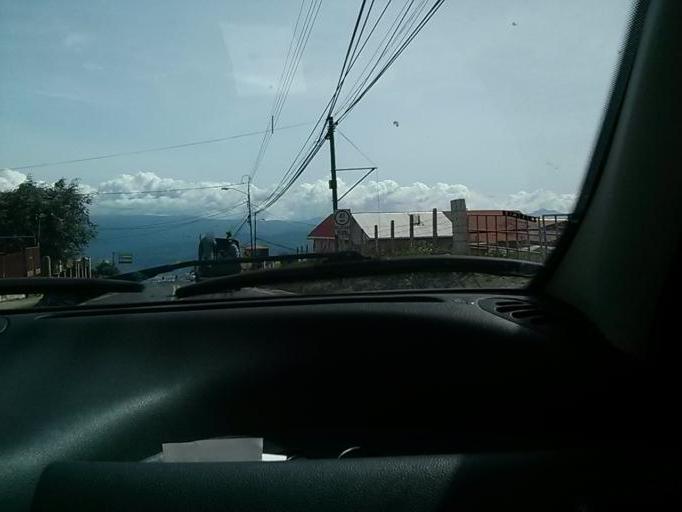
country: CR
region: Cartago
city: Cot
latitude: 9.9163
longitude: -83.8826
